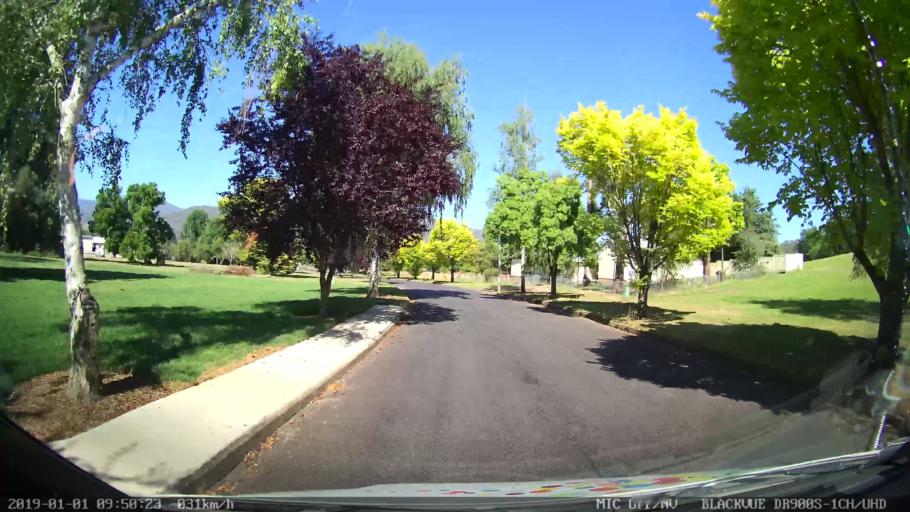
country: AU
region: New South Wales
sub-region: Snowy River
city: Jindabyne
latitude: -36.2164
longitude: 148.1265
